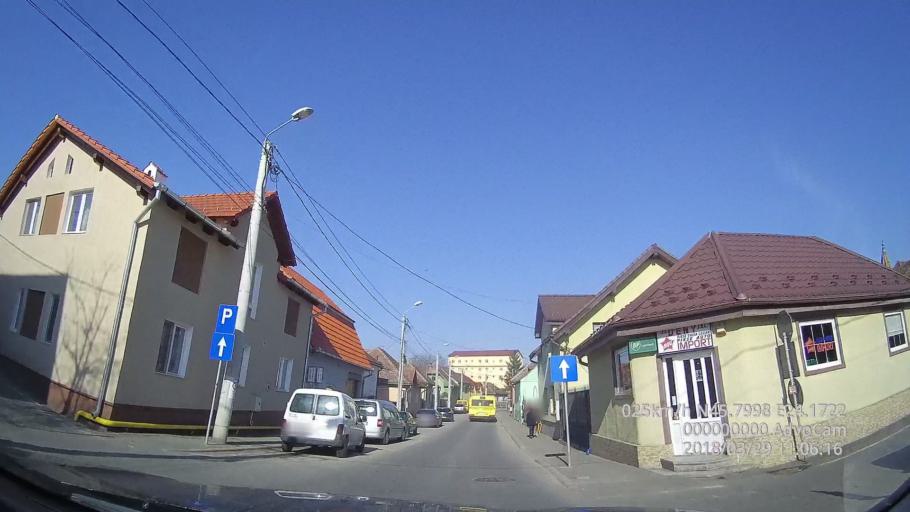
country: RO
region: Sibiu
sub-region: Municipiul Sibiu
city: Sibiu
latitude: 45.7999
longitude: 24.1718
